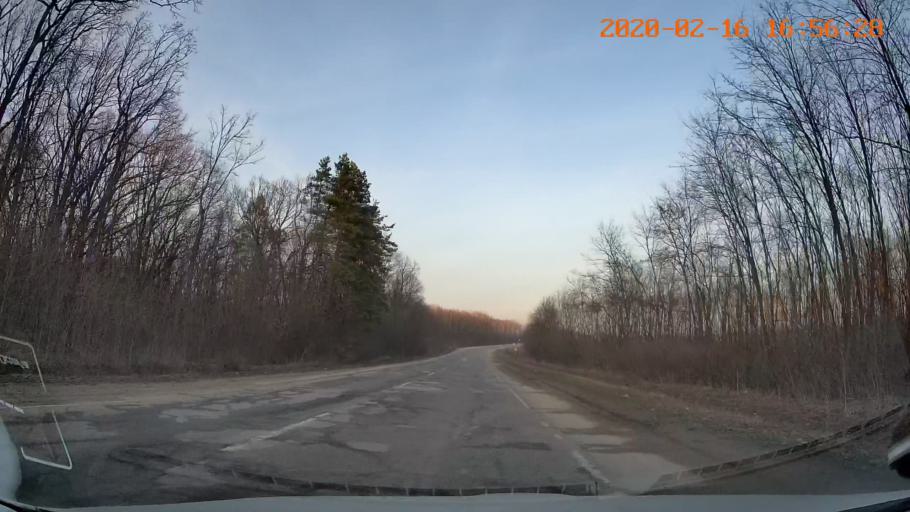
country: MD
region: Briceni
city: Briceni
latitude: 48.3334
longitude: 27.0505
